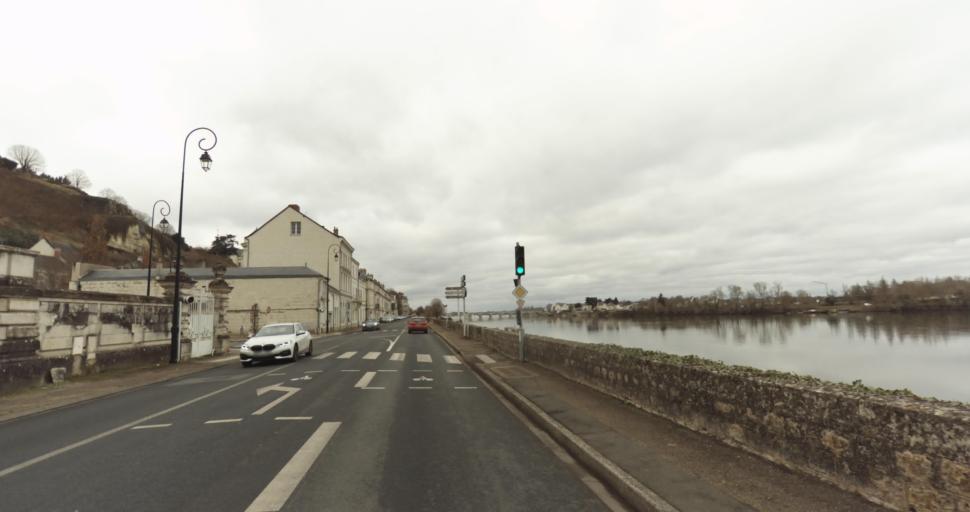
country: FR
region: Pays de la Loire
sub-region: Departement de Maine-et-Loire
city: Saumur
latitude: 47.2554
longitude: -0.0662
